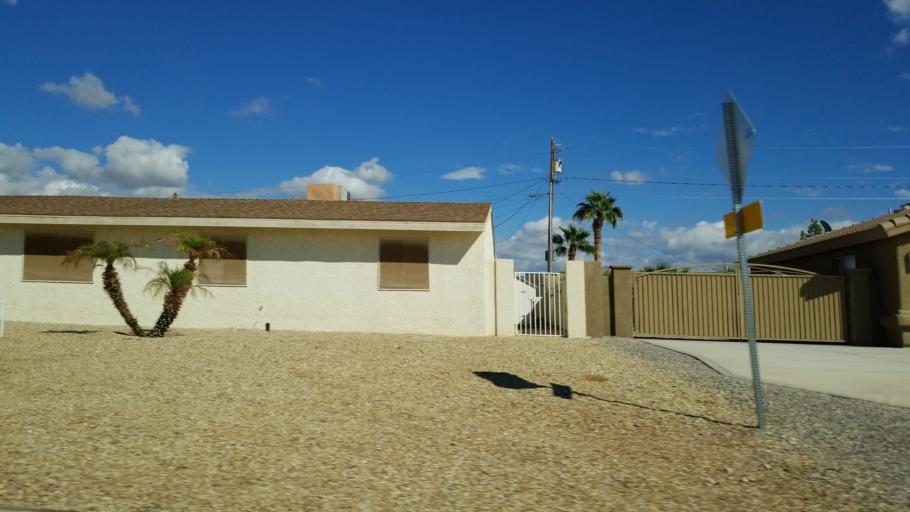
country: US
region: Arizona
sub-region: Mohave County
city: Lake Havasu City
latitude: 34.4780
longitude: -114.2672
